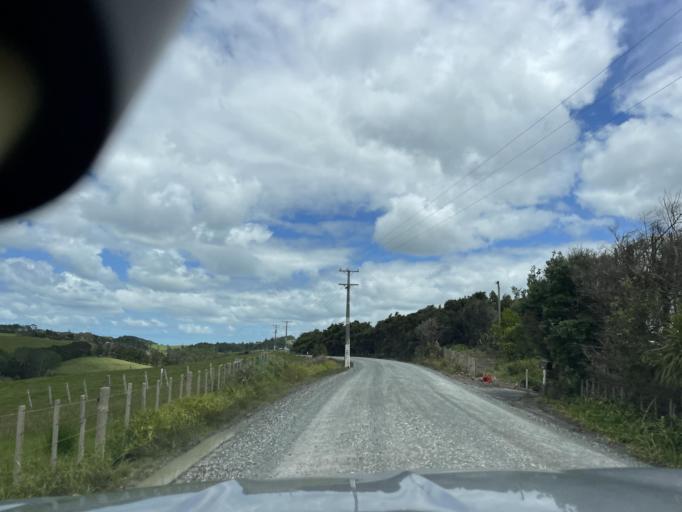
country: NZ
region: Auckland
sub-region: Auckland
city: Wellsford
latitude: -36.1728
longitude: 174.5760
